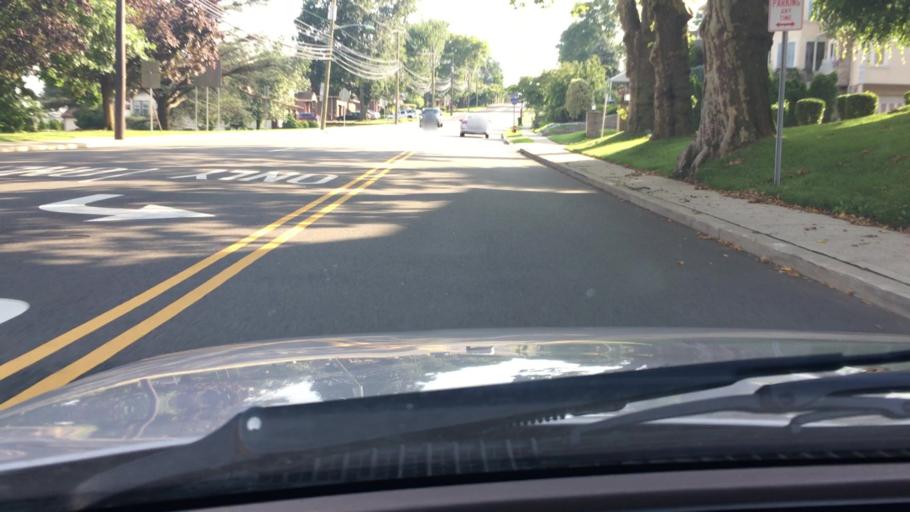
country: US
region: New Jersey
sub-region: Passaic County
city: Clifton
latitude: 40.8723
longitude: -74.1741
